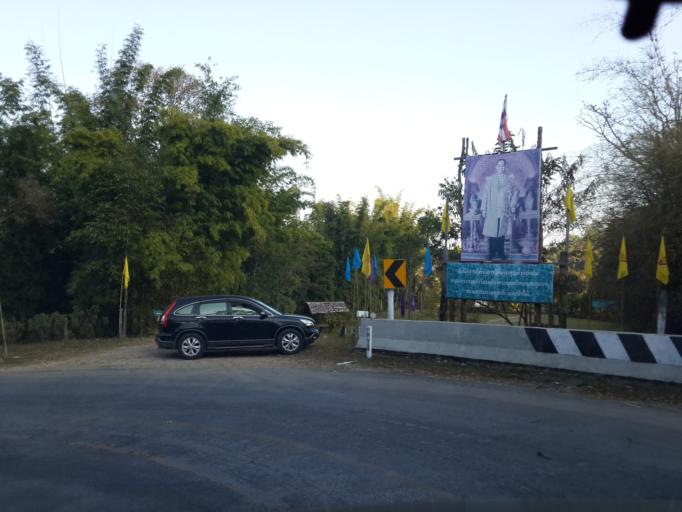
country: TH
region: Chiang Mai
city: Chai Prakan
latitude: 19.8510
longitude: 99.0633
